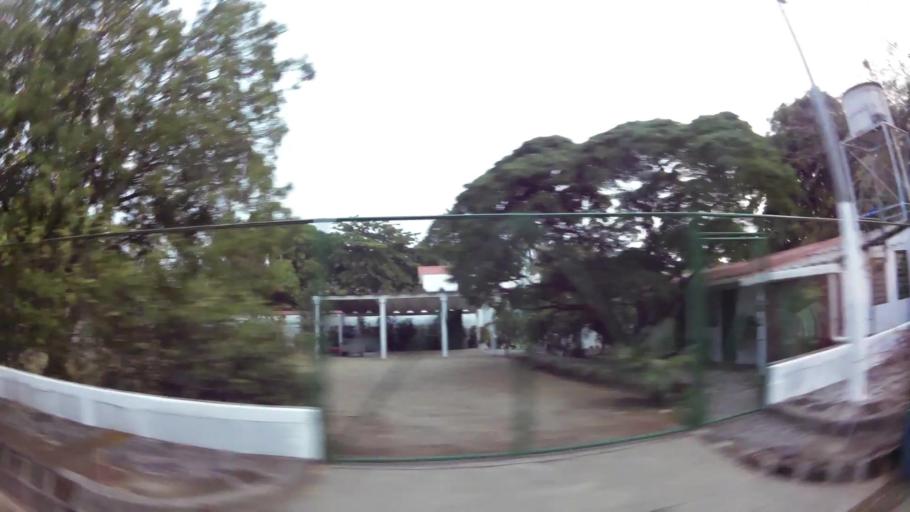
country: NI
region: Rivas
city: San Juan del Sur
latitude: 11.2621
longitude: -85.8791
